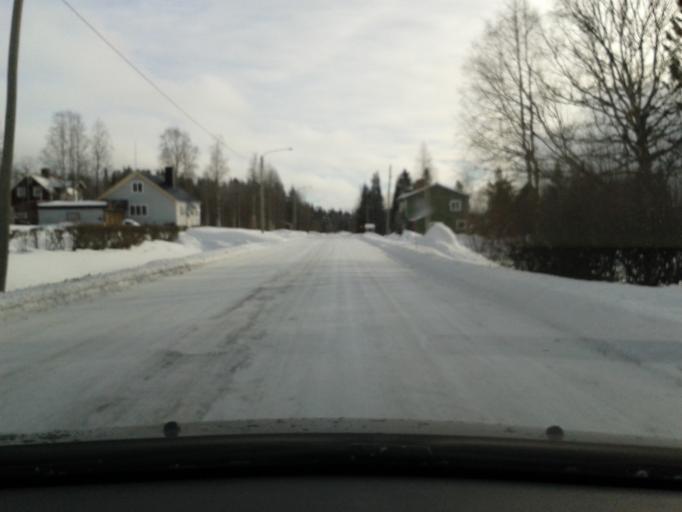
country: SE
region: Vaesterbotten
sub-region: Vilhelmina Kommun
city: Sjoberg
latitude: 64.6863
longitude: 16.2793
